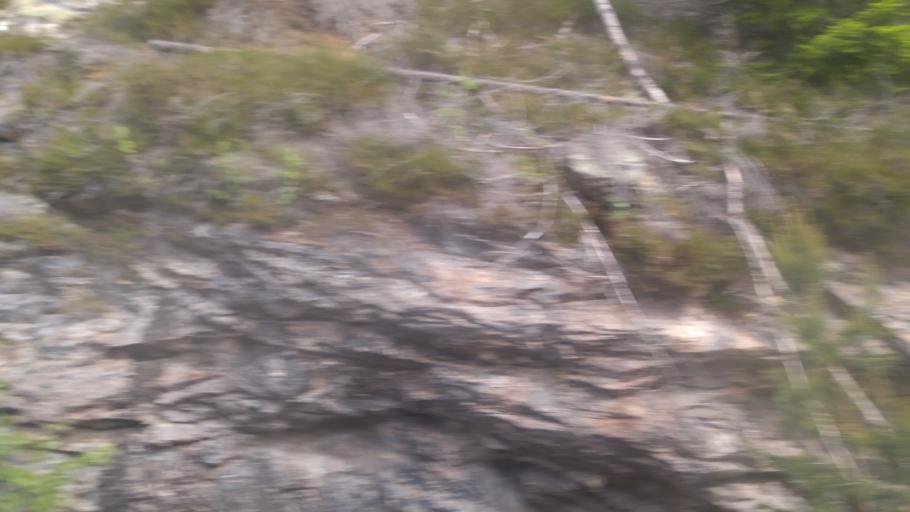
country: NO
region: Sor-Trondelag
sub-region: Selbu
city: Mebonden
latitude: 62.9711
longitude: 10.9475
